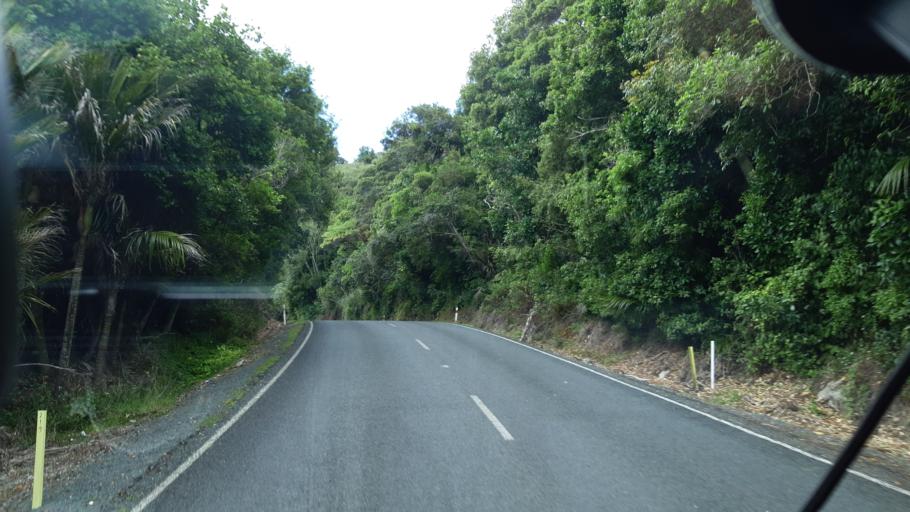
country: NZ
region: Northland
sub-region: Far North District
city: Taipa
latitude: -35.2469
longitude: 173.5307
